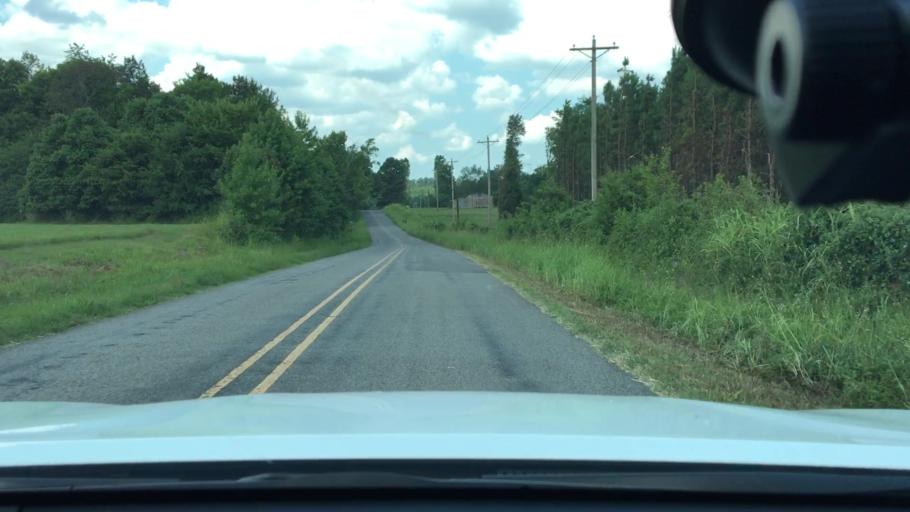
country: US
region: Arkansas
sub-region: Logan County
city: Paris
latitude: 35.2690
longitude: -93.6773
